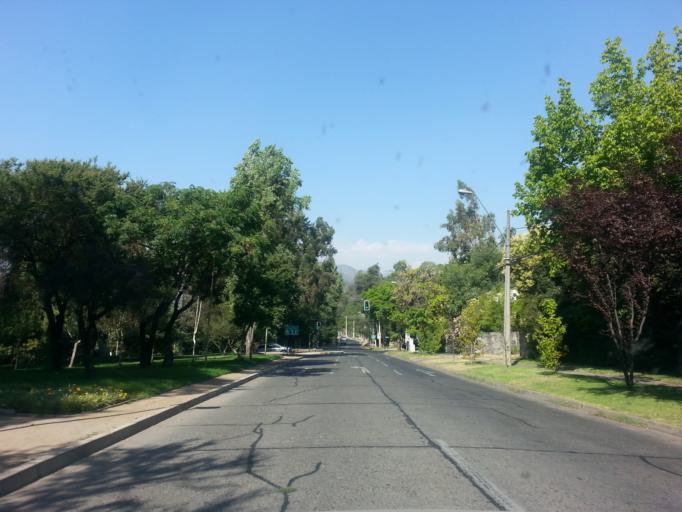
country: CL
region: Santiago Metropolitan
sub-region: Provincia de Santiago
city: Villa Presidente Frei, Nunoa, Santiago, Chile
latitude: -33.3865
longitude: -70.5221
